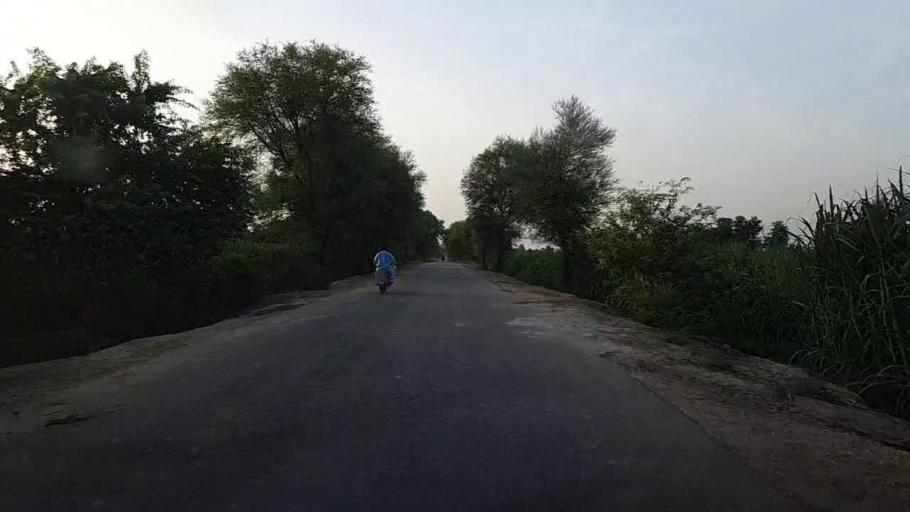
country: PK
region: Sindh
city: Ubauro
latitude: 28.2374
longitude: 69.8134
